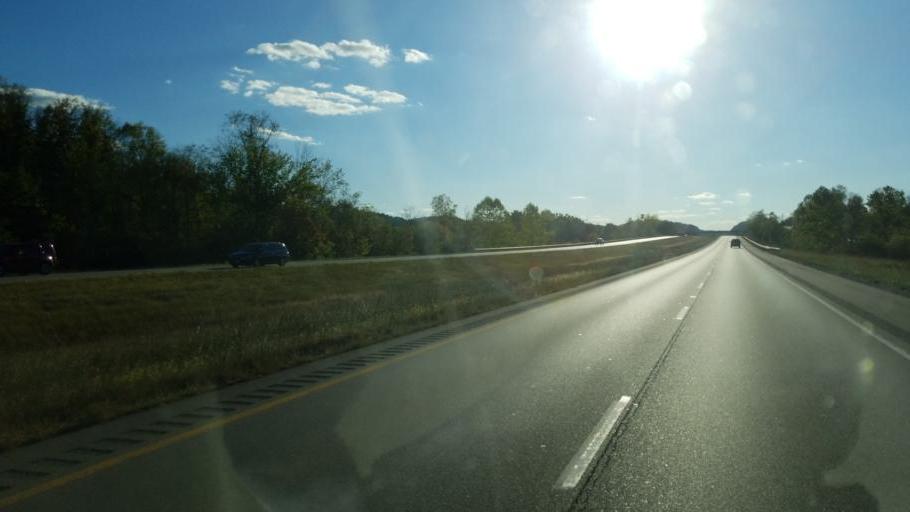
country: US
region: Ohio
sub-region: Belmont County
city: Barnesville
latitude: 40.0485
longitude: -81.3474
